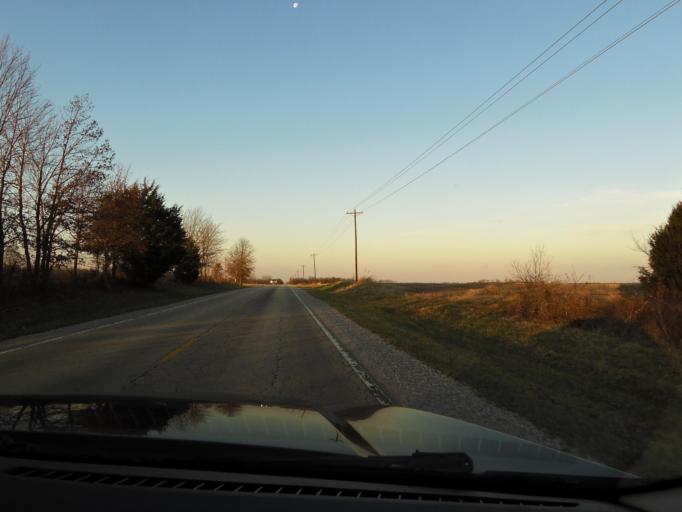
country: US
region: Illinois
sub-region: Marion County
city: Salem
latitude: 38.7654
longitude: -88.9656
